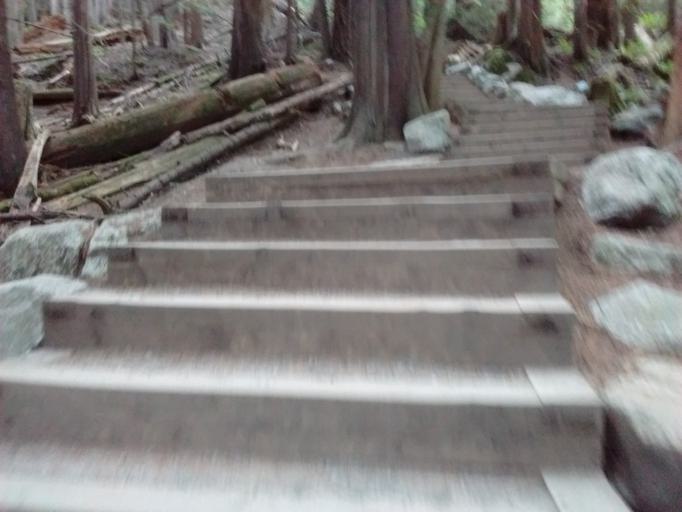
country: CA
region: British Columbia
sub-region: Greater Vancouver Regional District
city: Lions Bay
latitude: 49.6711
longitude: -123.1576
